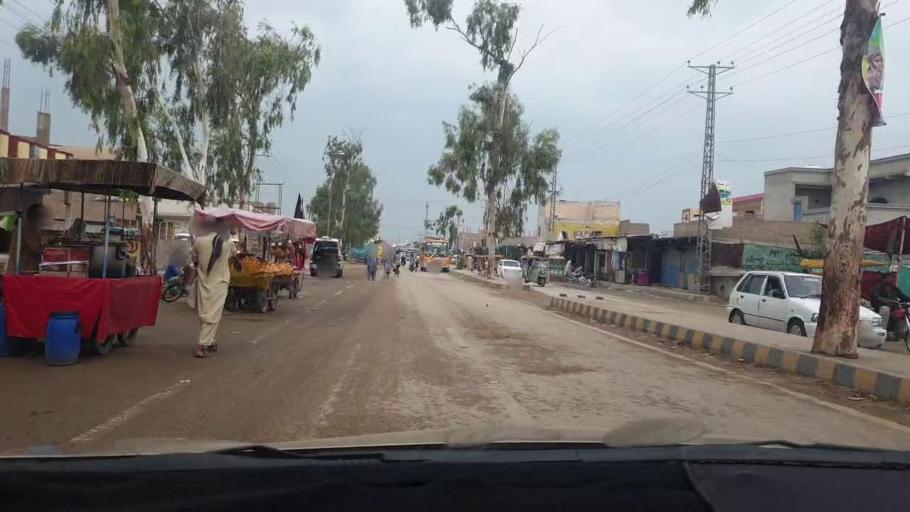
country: PK
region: Sindh
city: Larkana
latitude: 27.5796
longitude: 68.2222
